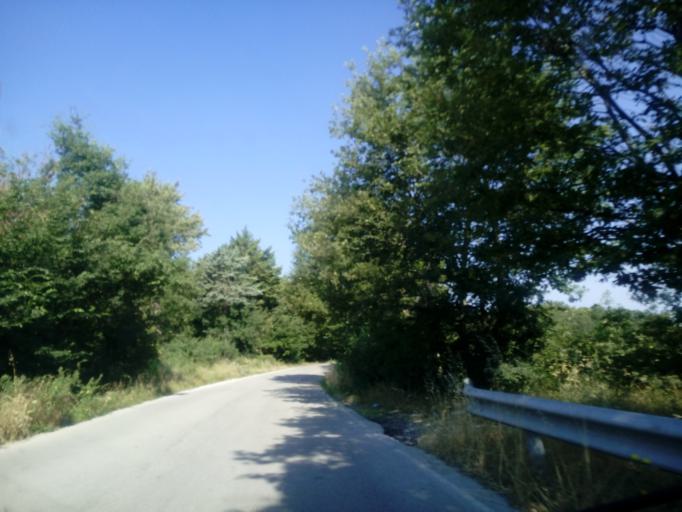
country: IT
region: Molise
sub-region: Provincia di Campobasso
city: Gildone
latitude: 41.5166
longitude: 14.7563
